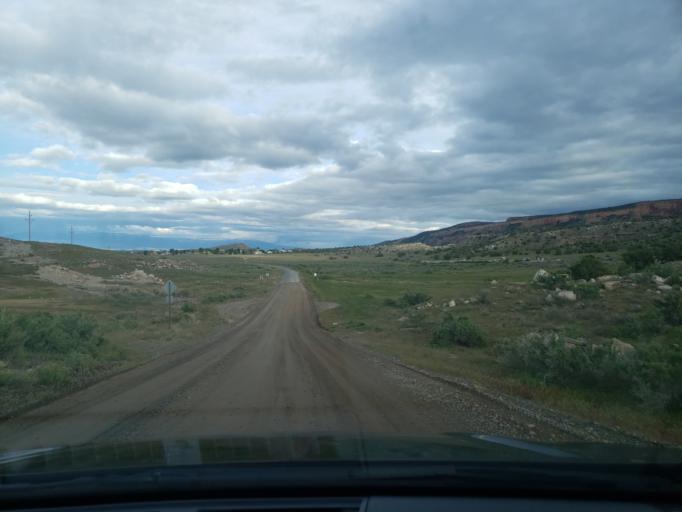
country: US
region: Colorado
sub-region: Mesa County
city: Fruita
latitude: 39.1427
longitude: -108.7584
